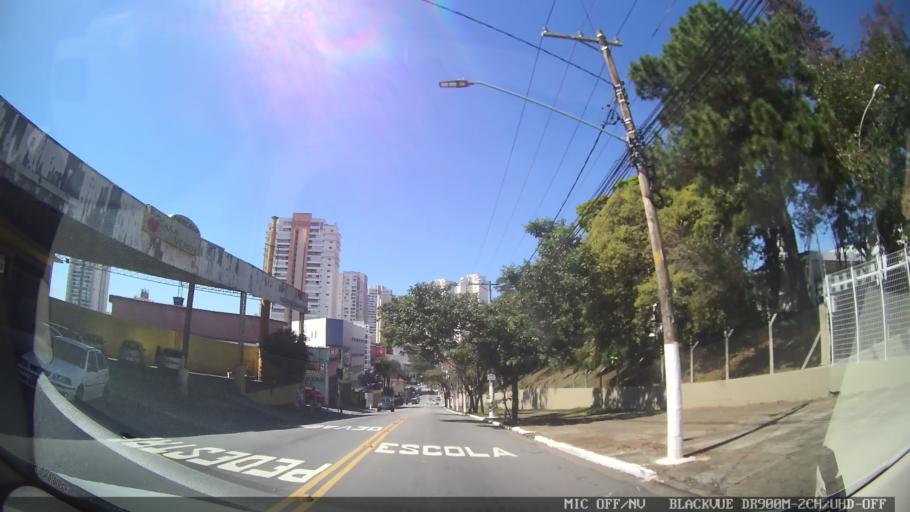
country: BR
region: Sao Paulo
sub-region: Sao Paulo
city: Sao Paulo
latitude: -23.4999
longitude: -46.6462
